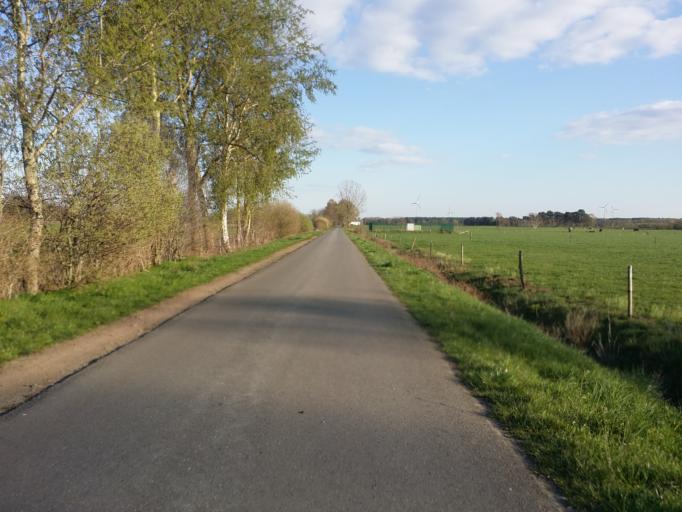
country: DE
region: Lower Saxony
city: Delmenhorst
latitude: 53.0103
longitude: 8.6325
